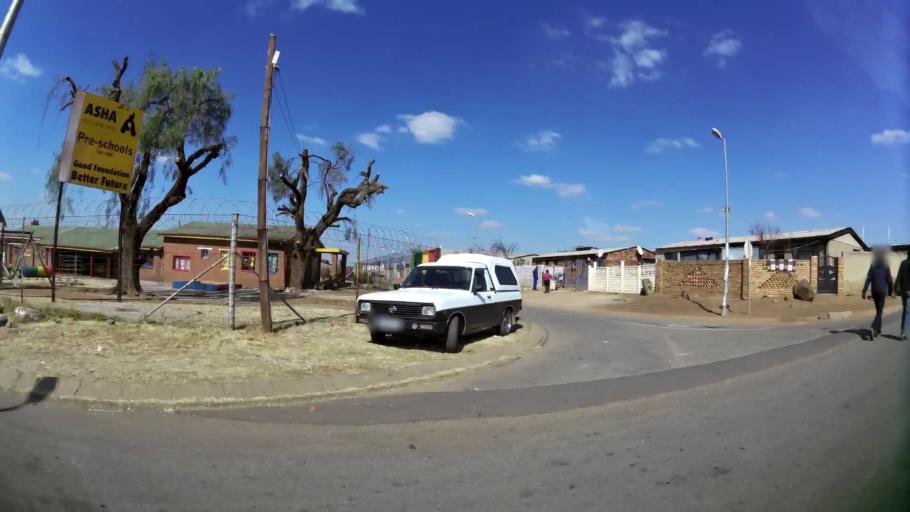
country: ZA
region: Gauteng
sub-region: City of Johannesburg Metropolitan Municipality
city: Soweto
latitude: -26.2480
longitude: 27.8847
